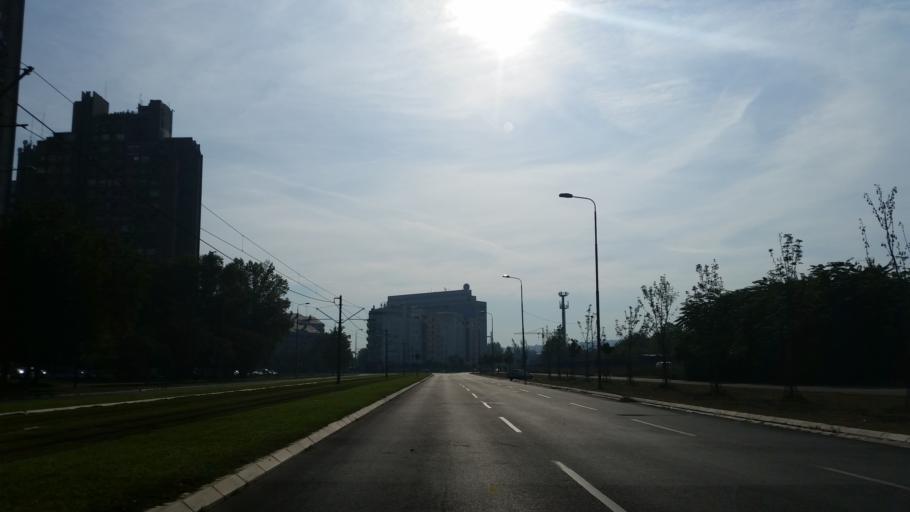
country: RS
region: Central Serbia
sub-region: Belgrade
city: Novi Beograd
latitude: 44.8065
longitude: 20.4231
